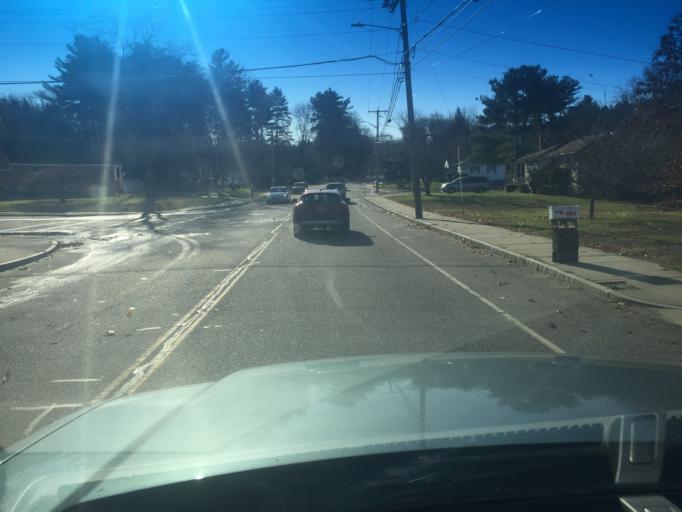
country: US
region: Massachusetts
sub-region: Norfolk County
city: Franklin
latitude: 42.1118
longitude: -71.4293
